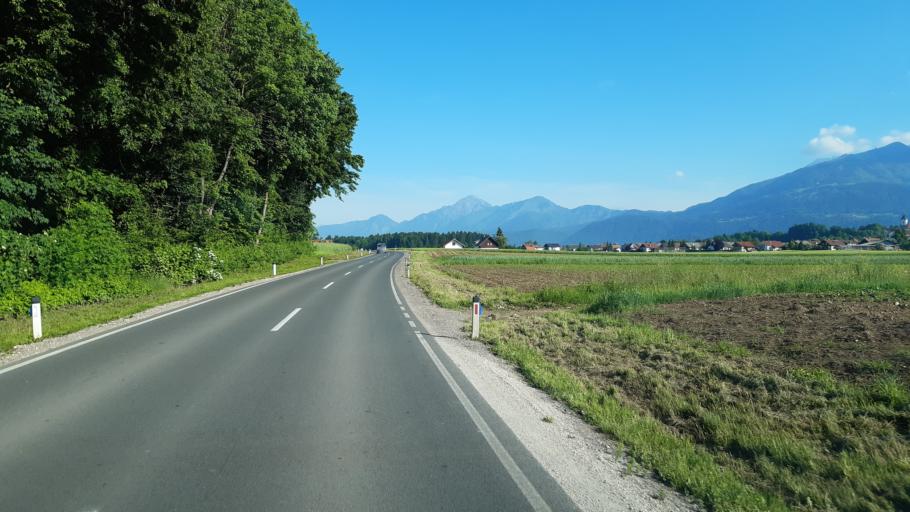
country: SI
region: Komenda
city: Komenda
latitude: 46.1980
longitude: 14.5393
